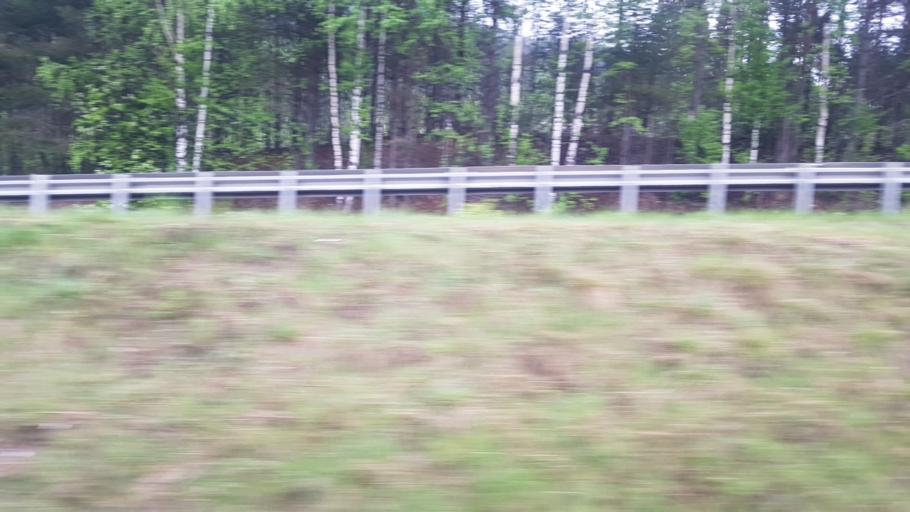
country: NO
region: Oppland
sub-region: Nord-Fron
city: Vinstra
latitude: 61.6062
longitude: 9.7136
